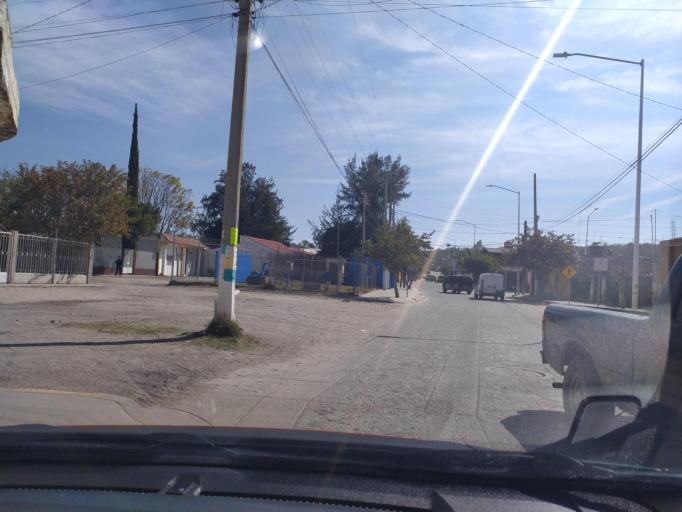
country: MX
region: Guanajuato
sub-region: San Francisco del Rincon
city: San Ignacio de Hidalgo
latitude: 20.8811
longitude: -101.8562
